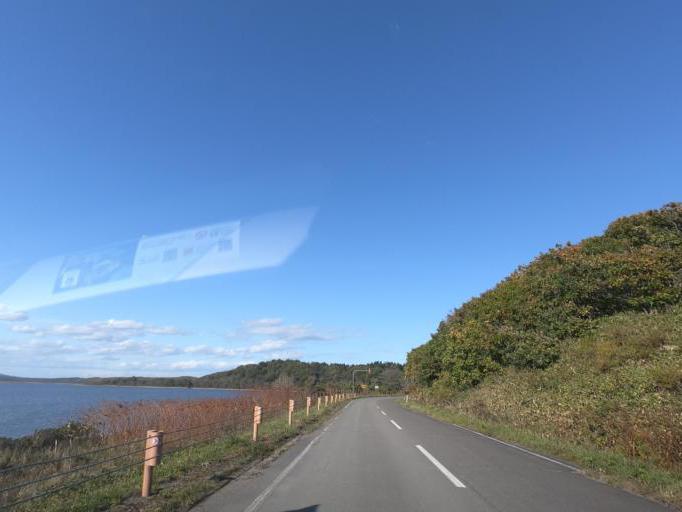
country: JP
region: Hokkaido
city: Obihiro
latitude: 42.6012
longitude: 143.5498
